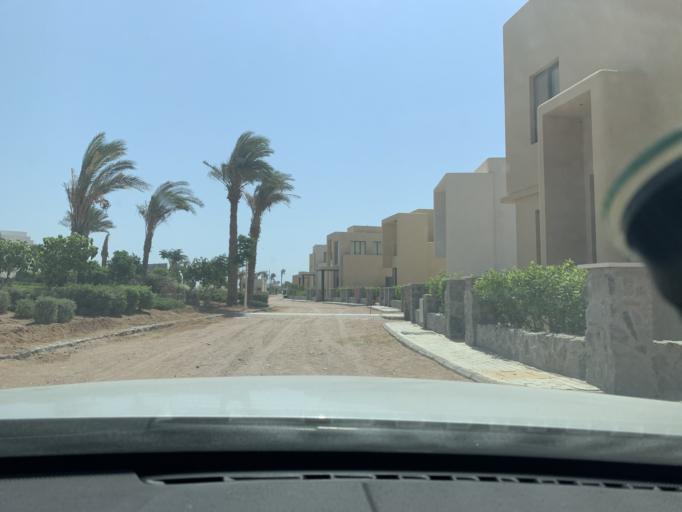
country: EG
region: Red Sea
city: El Gouna
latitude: 27.4038
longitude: 33.6587
